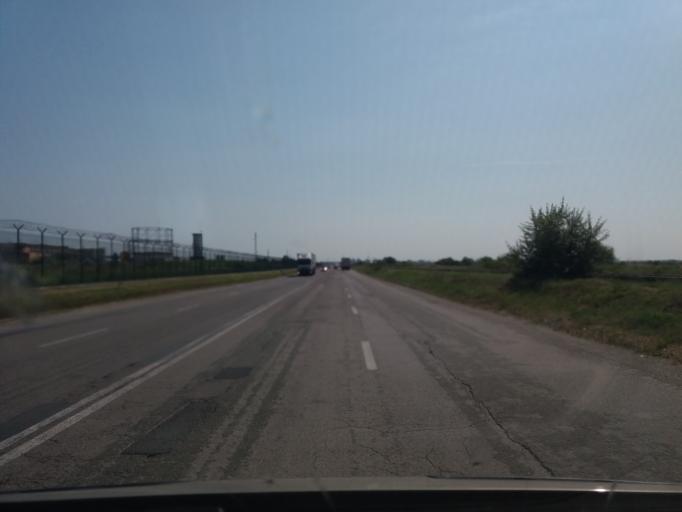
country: RO
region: Constanta
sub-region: Comuna Corbu
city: Corbu
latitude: 44.3433
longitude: 28.6410
